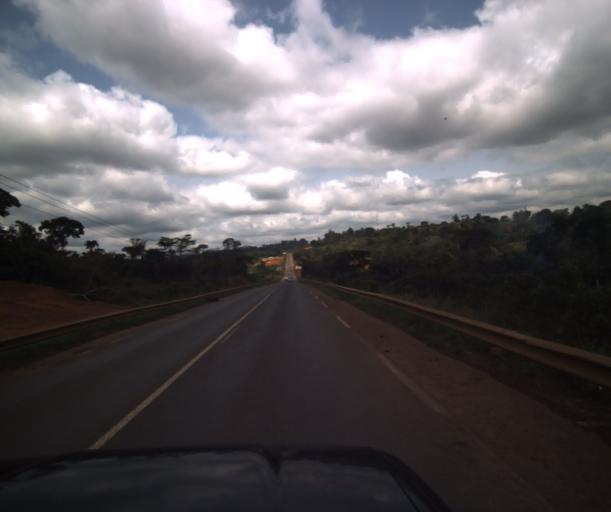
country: CM
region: Centre
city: Mbankomo
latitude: 3.7849
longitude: 11.4571
